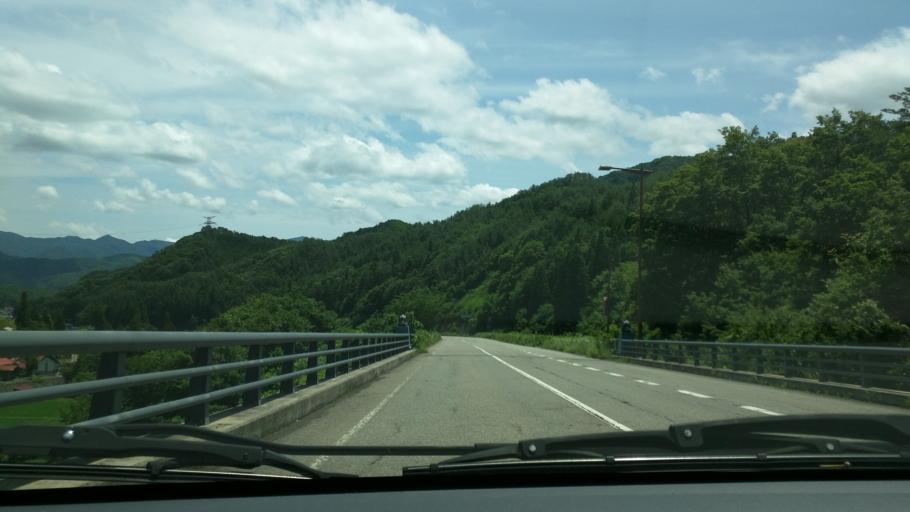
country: JP
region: Tochigi
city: Kuroiso
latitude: 37.2299
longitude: 139.7374
